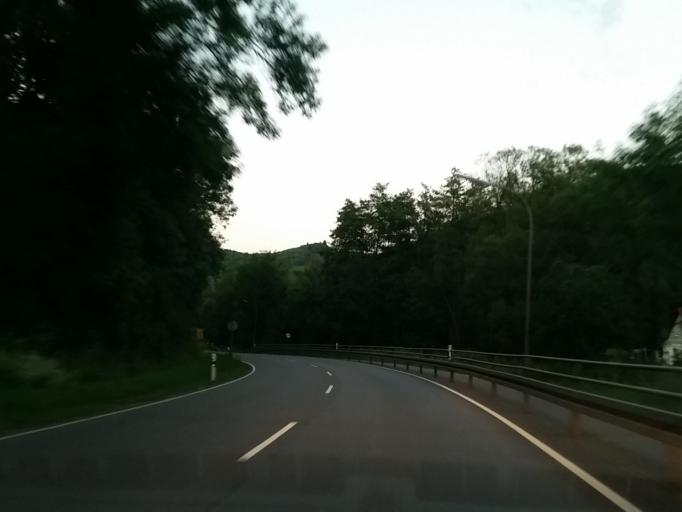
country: DE
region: Saarland
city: Schmelz
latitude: 49.4622
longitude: 6.8450
